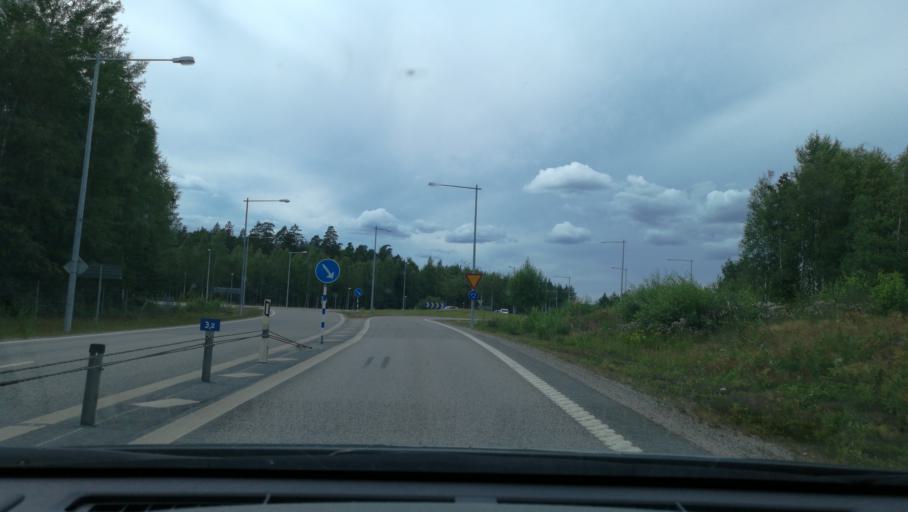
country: SE
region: OEstergoetland
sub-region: Norrkopings Kommun
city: Jursla
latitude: 58.6356
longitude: 16.1039
